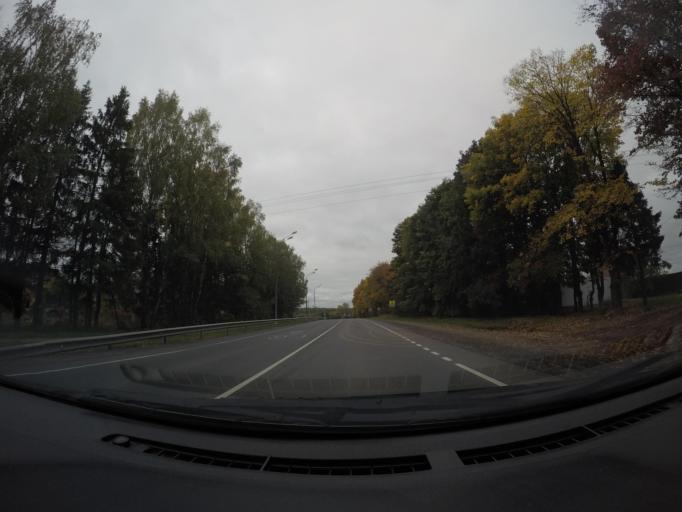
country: RU
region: Moskovskaya
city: Ruza
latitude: 55.7379
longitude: 36.2227
